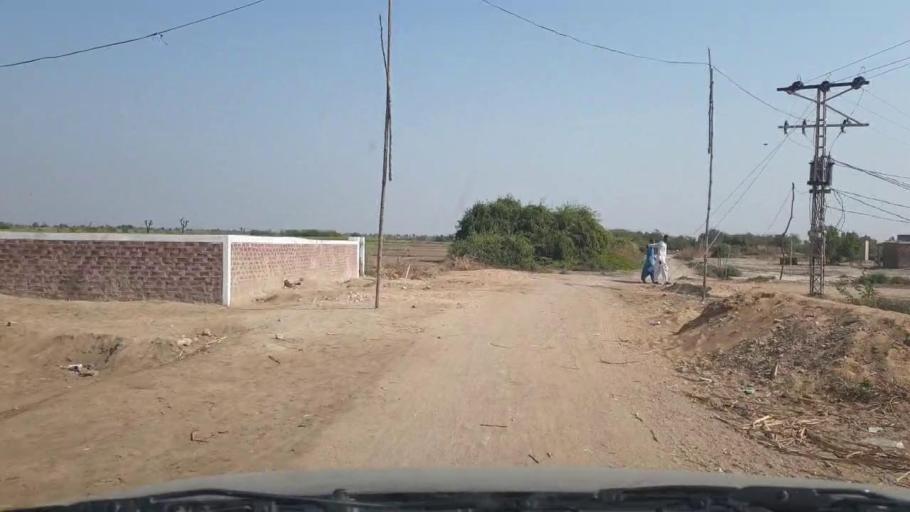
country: PK
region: Sindh
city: Samaro
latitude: 25.1790
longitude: 69.3378
